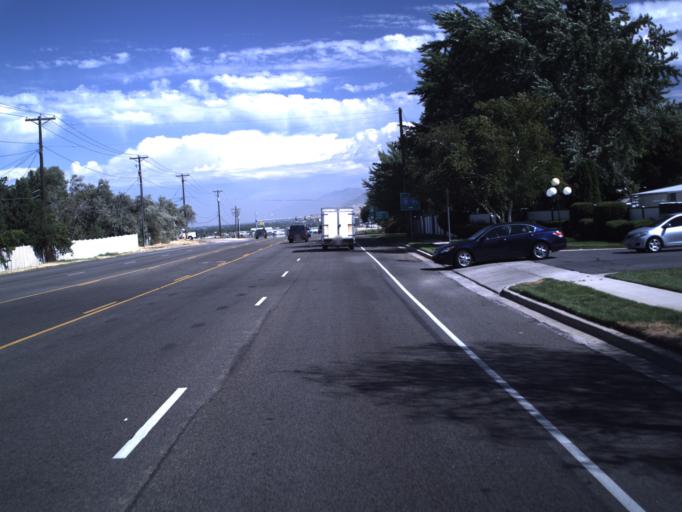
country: US
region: Utah
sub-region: Weber County
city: West Haven
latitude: 41.1948
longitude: -112.0257
